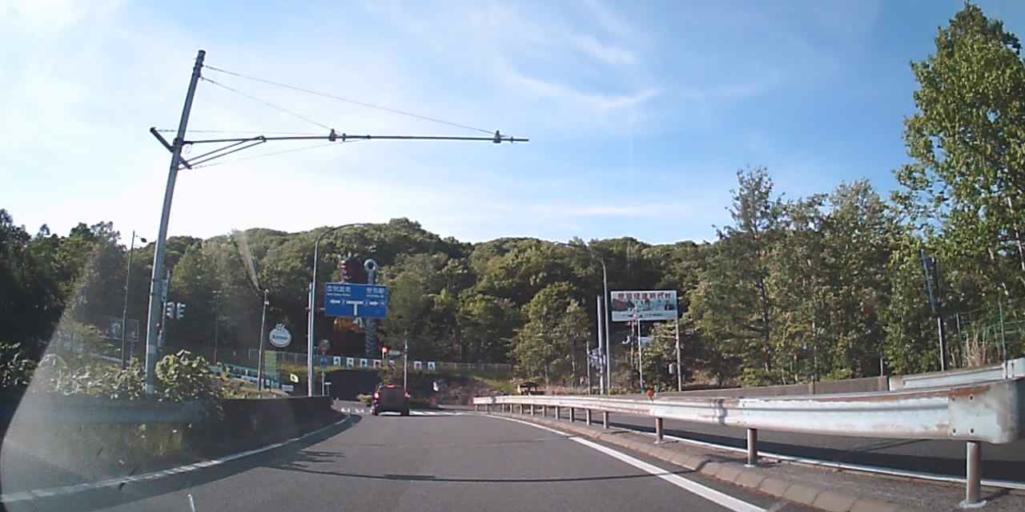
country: JP
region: Hokkaido
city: Shiraoi
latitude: 42.4648
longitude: 141.1738
